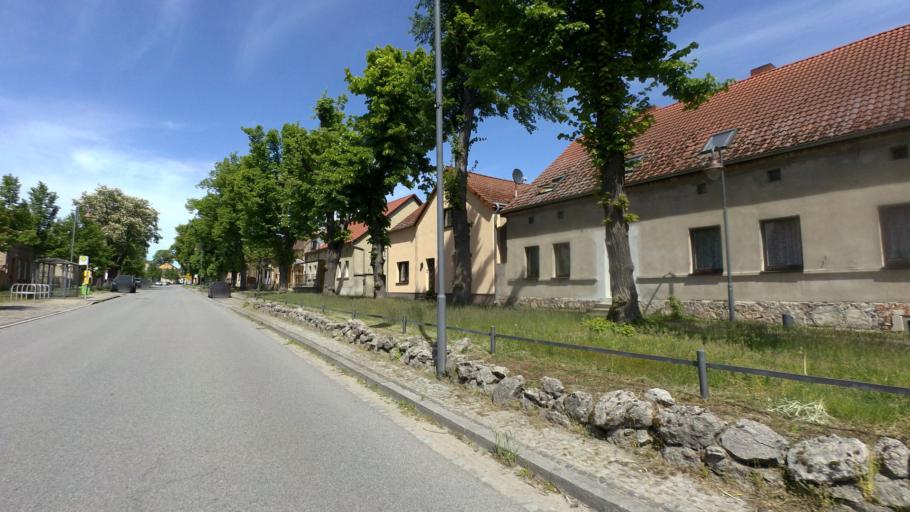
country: DE
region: Brandenburg
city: Sperenberg
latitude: 52.1385
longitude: 13.3656
